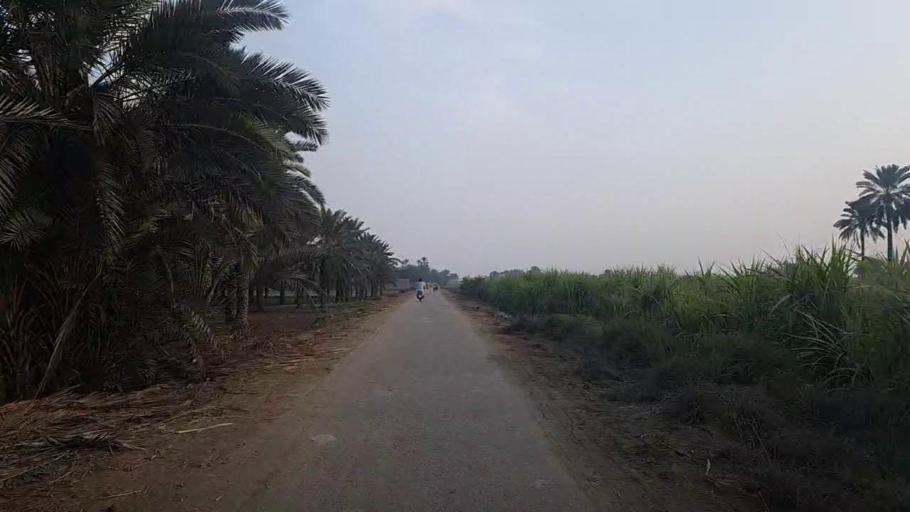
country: PK
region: Sindh
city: Kot Diji
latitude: 27.3822
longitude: 68.6628
